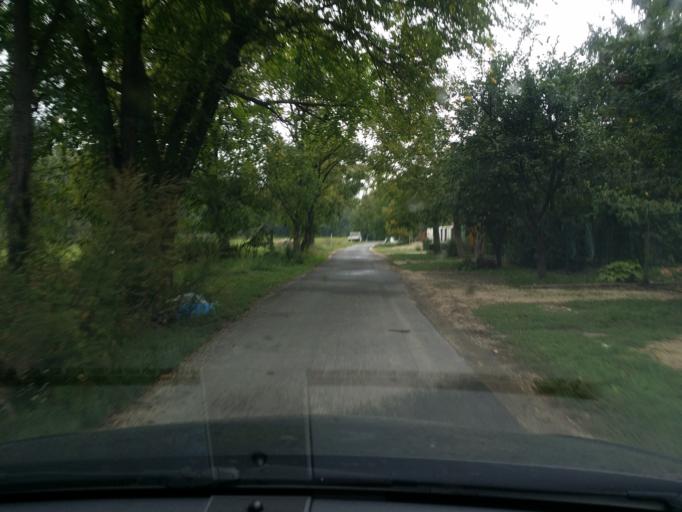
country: HU
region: Pest
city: Szigetcsep
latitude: 47.2349
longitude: 18.9687
